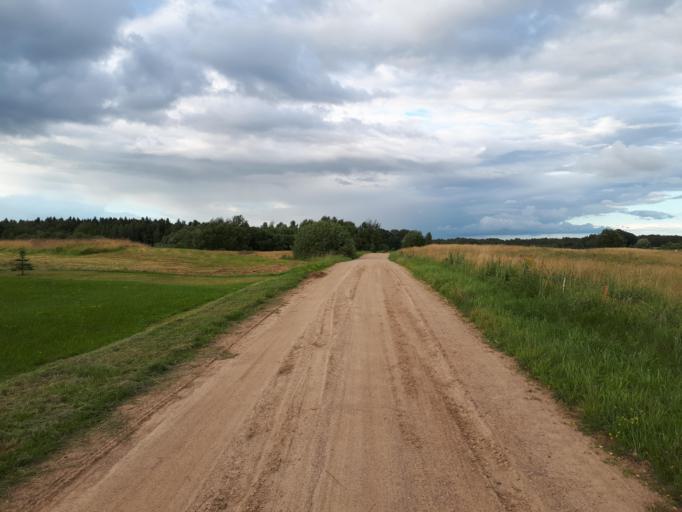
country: LT
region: Alytaus apskritis
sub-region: Alytaus rajonas
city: Daugai
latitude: 54.4654
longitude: 24.2326
